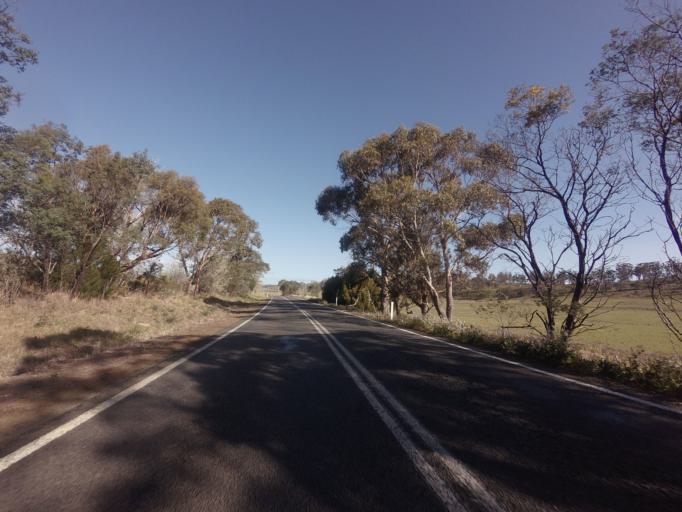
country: AU
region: Tasmania
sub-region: Sorell
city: Sorell
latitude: -42.4690
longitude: 147.9233
